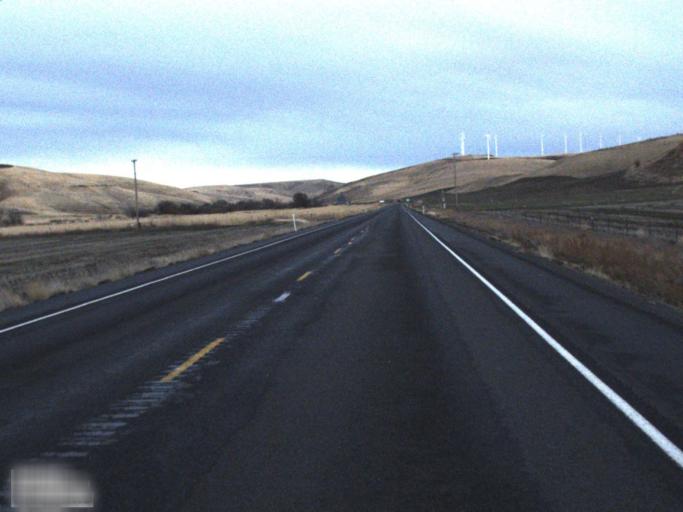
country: US
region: Washington
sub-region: Columbia County
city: Dayton
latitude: 46.5316
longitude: -117.8445
